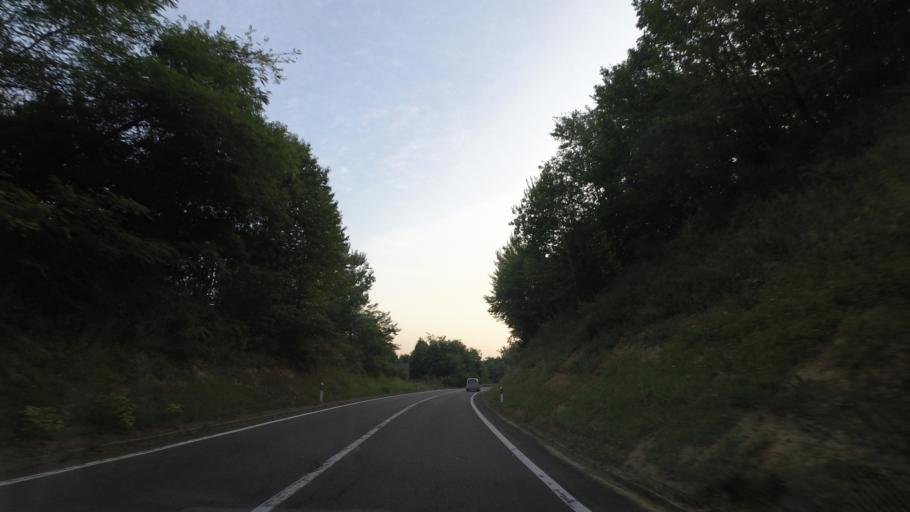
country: HR
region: Brodsko-Posavska
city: Cernik
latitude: 45.2779
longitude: 17.4024
